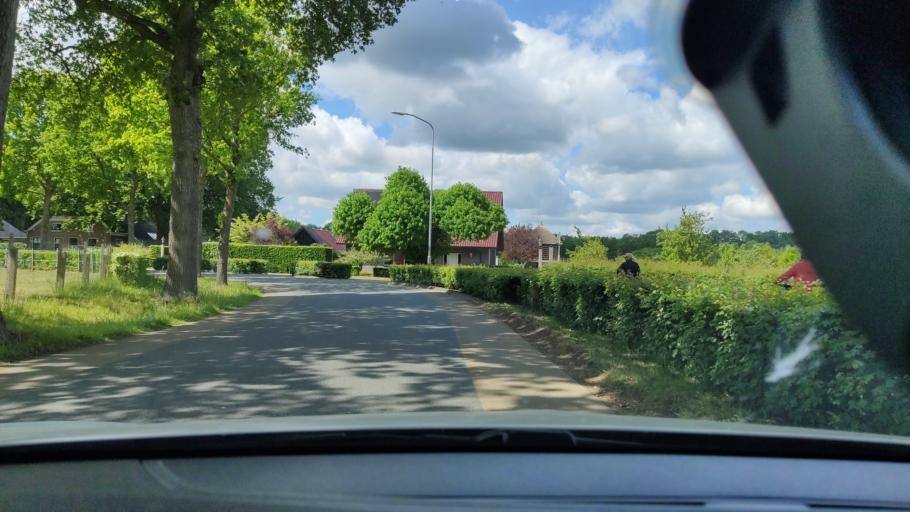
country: NL
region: Drenthe
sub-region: Gemeente Tynaarlo
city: Zuidlaren
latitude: 53.1091
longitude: 6.6807
